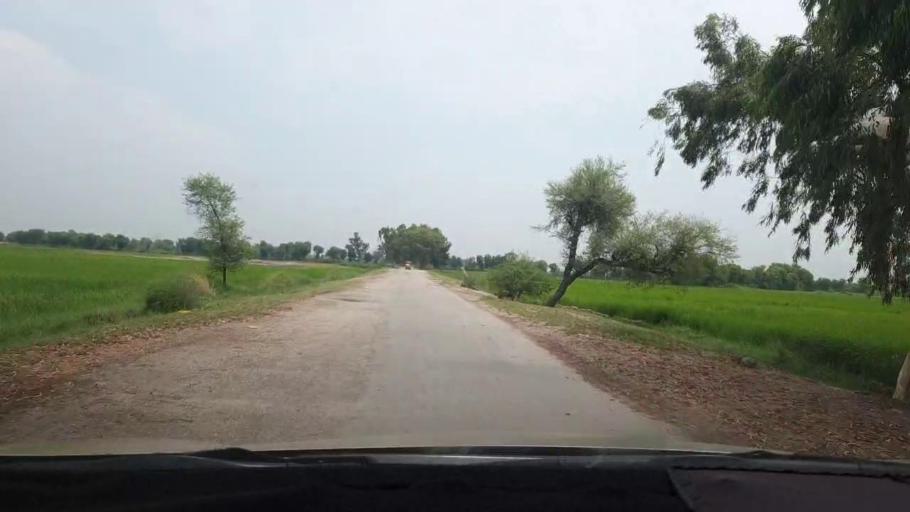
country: PK
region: Sindh
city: Ratodero
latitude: 27.7576
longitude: 68.3161
